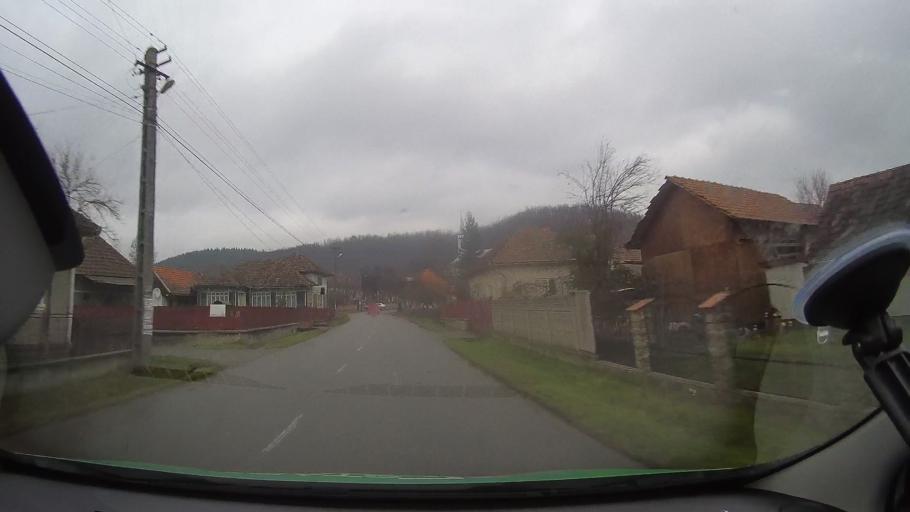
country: RO
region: Hunedoara
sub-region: Comuna Tomesti
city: Tomesti
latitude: 46.1967
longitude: 22.6418
